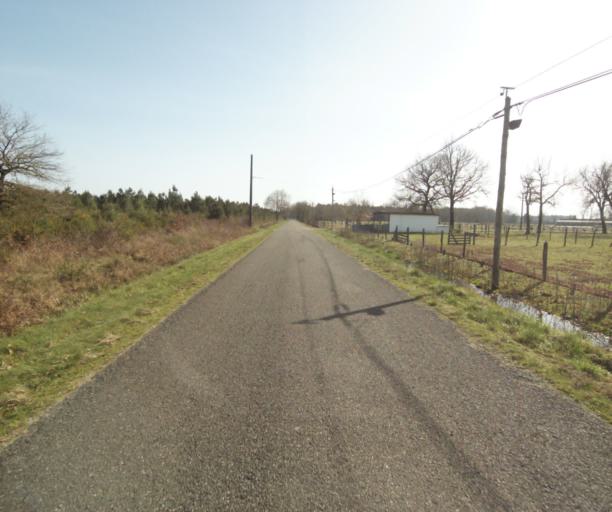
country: FR
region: Aquitaine
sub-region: Departement des Landes
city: Roquefort
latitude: 44.1377
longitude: -0.2605
